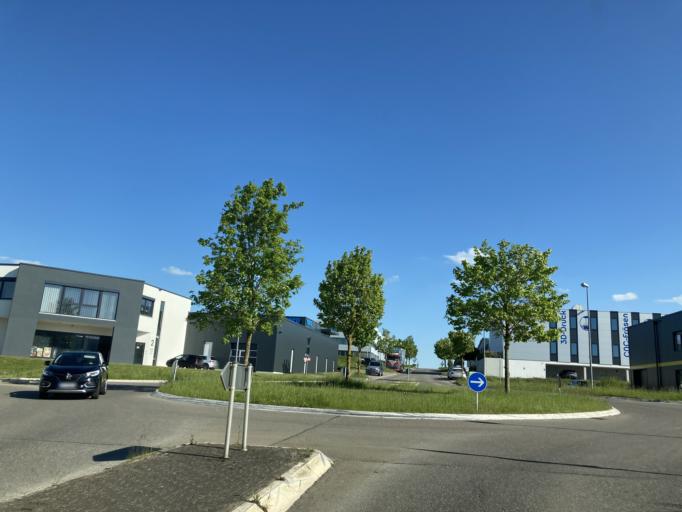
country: DE
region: Baden-Wuerttemberg
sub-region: Freiburg Region
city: Zimmern ob Rottweil
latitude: 48.1682
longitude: 8.5651
